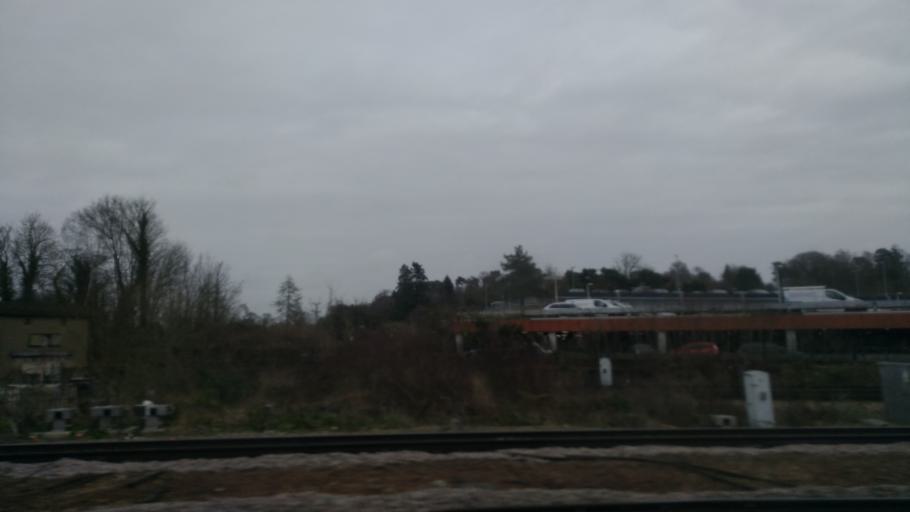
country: GB
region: England
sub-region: Kent
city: Sevenoaks
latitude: 51.2789
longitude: 0.1803
